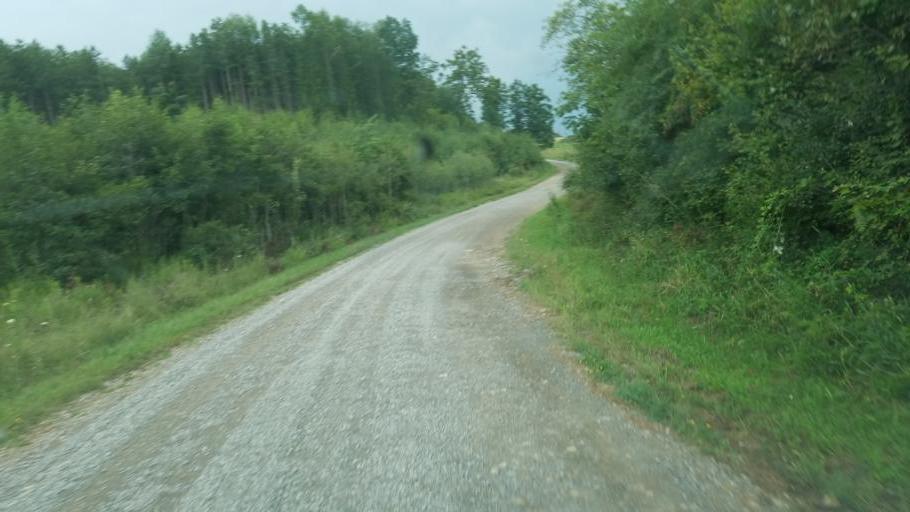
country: US
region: Pennsylvania
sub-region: Clarion County
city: Knox
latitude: 41.1479
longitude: -79.4922
